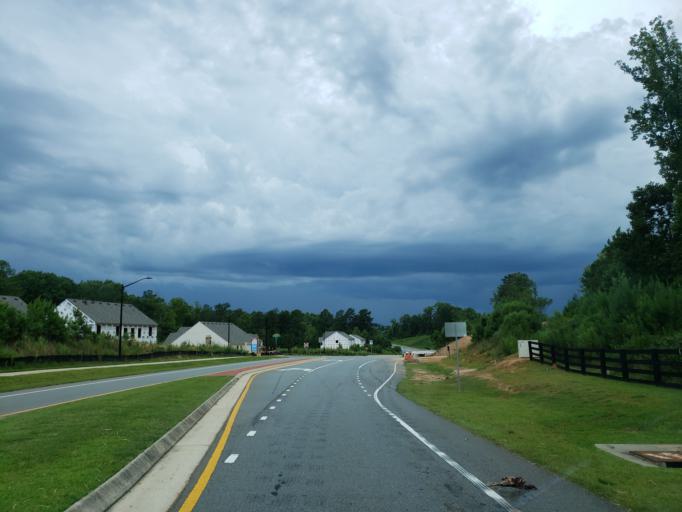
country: US
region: Georgia
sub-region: Cobb County
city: Acworth
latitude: 34.0290
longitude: -84.7585
